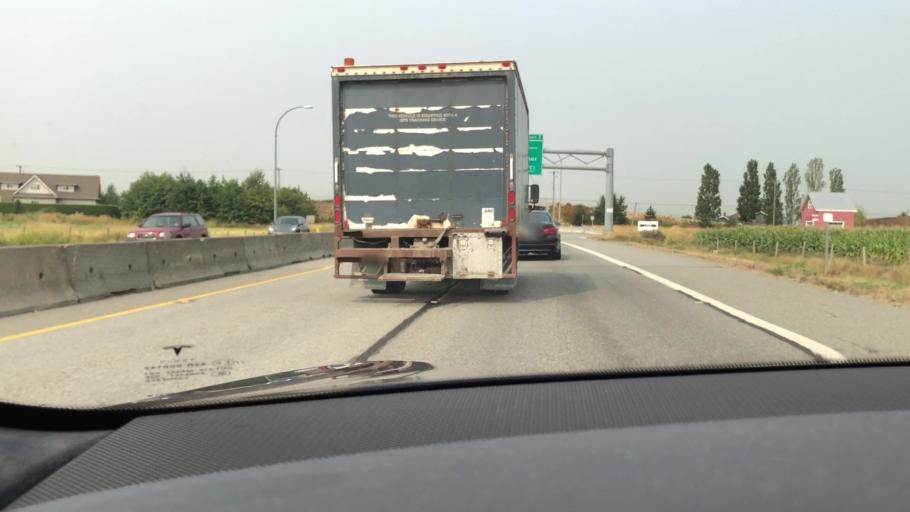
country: CA
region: British Columbia
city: Ladner
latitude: 49.0519
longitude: -123.0574
